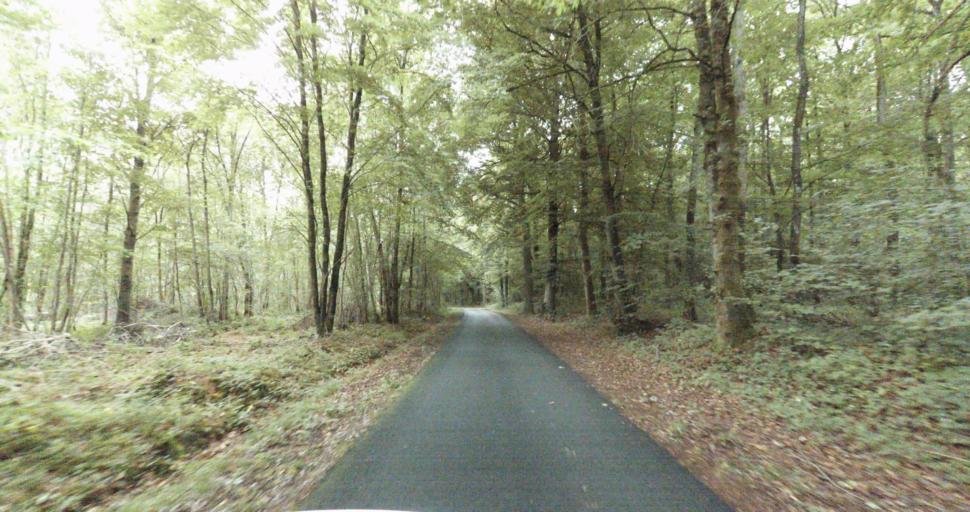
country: FR
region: Lower Normandy
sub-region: Departement de l'Orne
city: Vimoutiers
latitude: 48.9019
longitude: 0.1121
